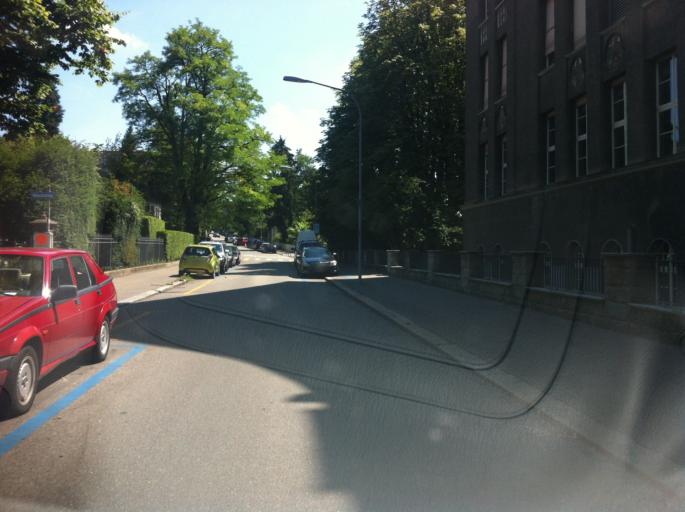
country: CH
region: Zurich
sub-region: Bezirk Zuerich
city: Zuerich (Kreis 8) / Muehlebach
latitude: 47.3566
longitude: 8.5587
